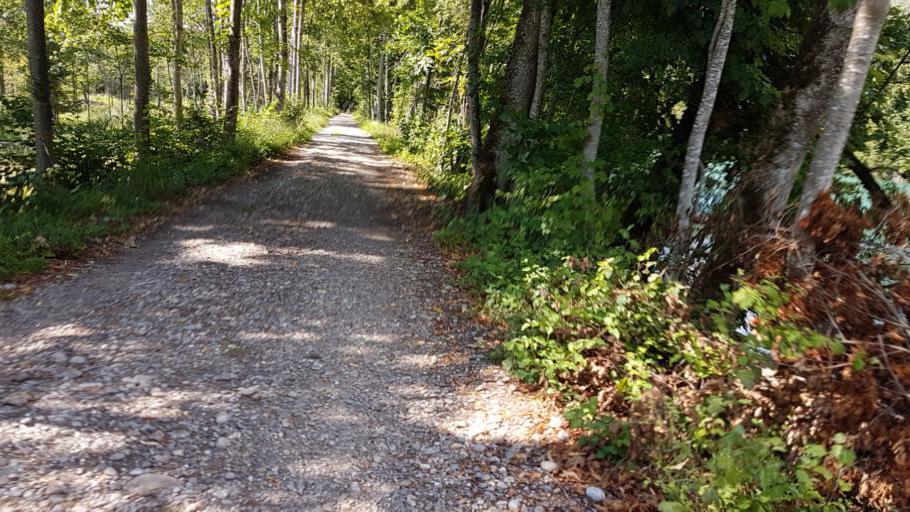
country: CH
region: Bern
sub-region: Bern-Mittelland District
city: Muri
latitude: 46.9168
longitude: 7.5023
